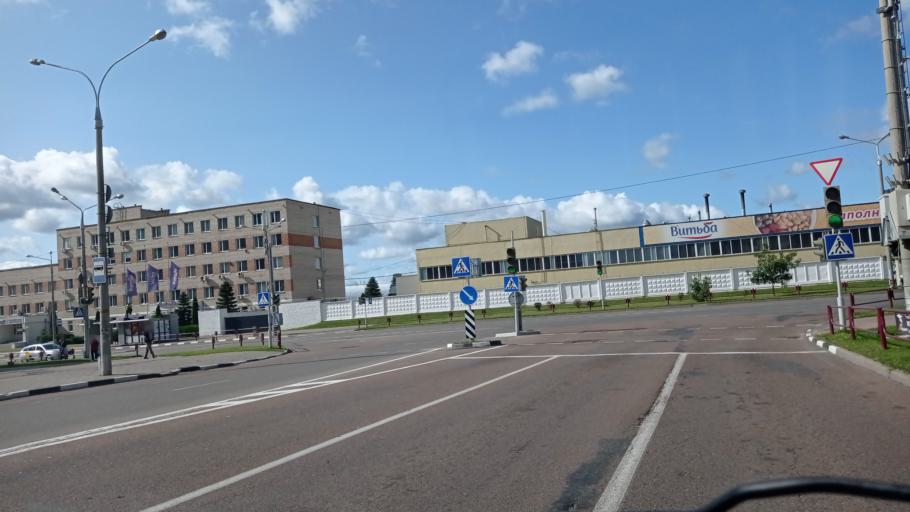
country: BY
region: Vitebsk
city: Vitebsk
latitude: 55.1702
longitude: 30.2578
